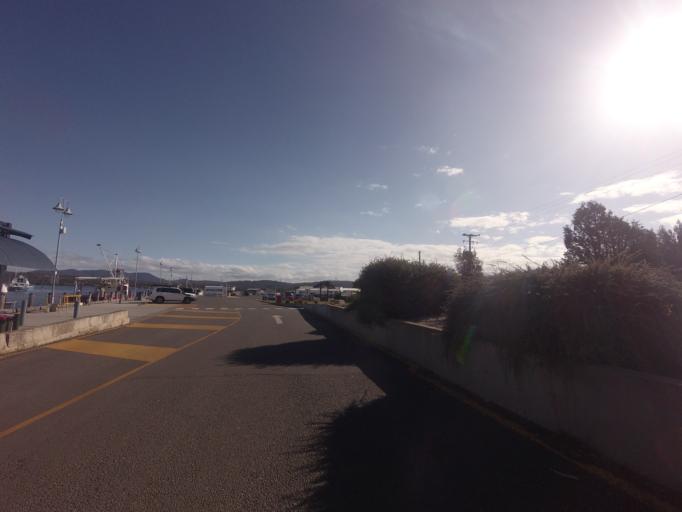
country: AU
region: Tasmania
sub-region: Sorell
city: Sorell
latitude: -42.5097
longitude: 147.9153
